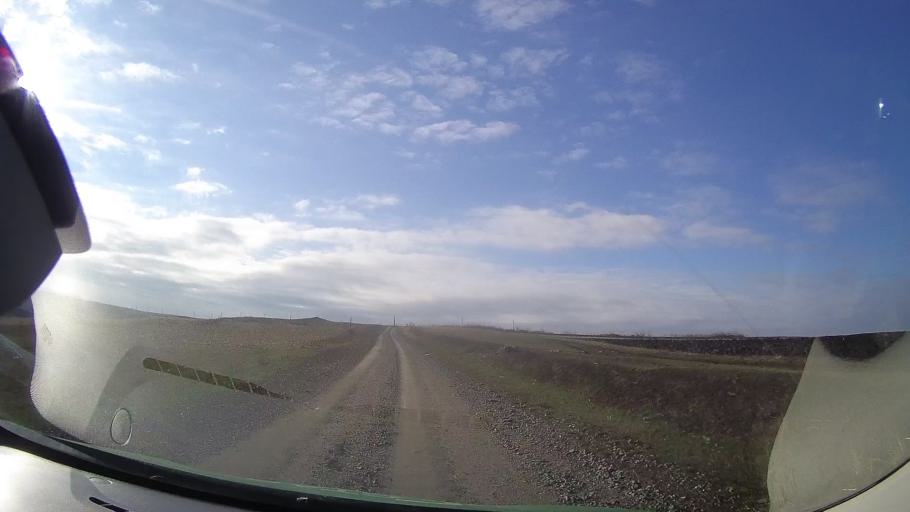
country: RO
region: Mures
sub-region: Comuna Saulia
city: Saulia
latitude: 46.5975
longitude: 24.2224
